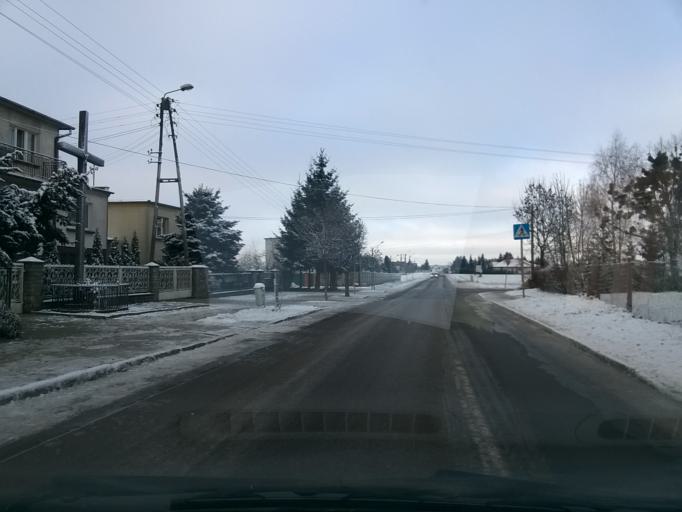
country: PL
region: Kujawsko-Pomorskie
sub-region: Powiat nakielski
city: Kcynia
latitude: 52.9953
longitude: 17.4785
